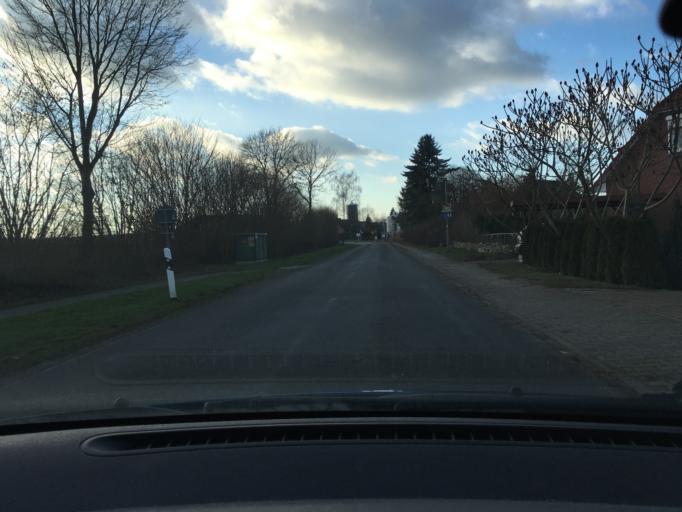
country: DE
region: Schleswig-Holstein
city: Schulendorf
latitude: 53.4759
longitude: 10.5456
